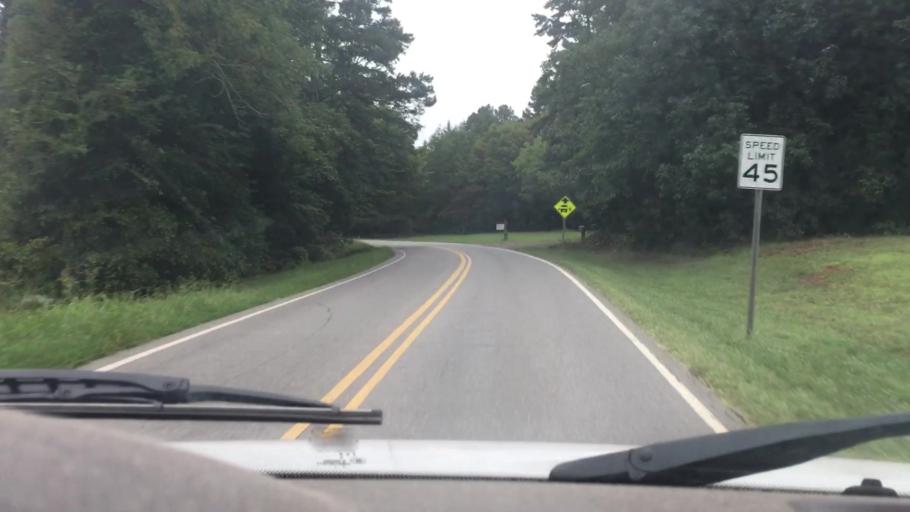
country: US
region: North Carolina
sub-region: Gaston County
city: Davidson
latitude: 35.5243
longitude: -80.7991
